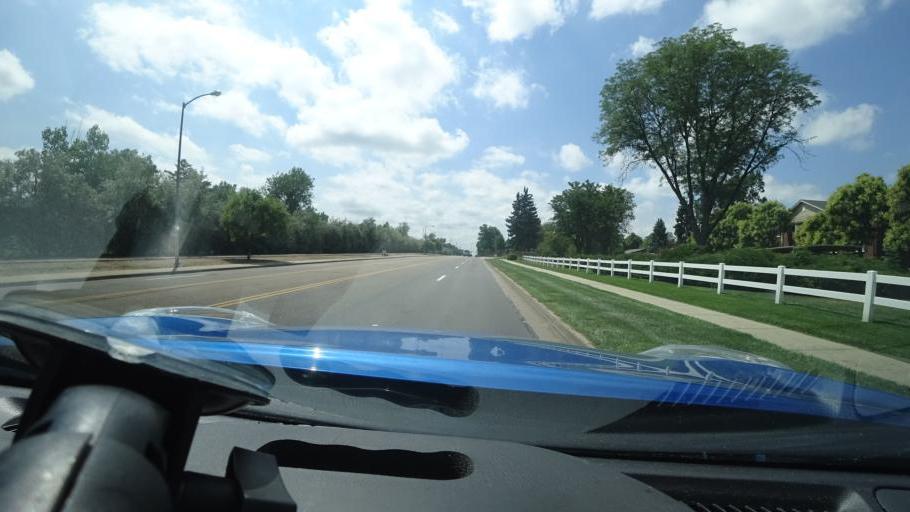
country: US
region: Colorado
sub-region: Adams County
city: Aurora
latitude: 39.7144
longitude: -104.8472
